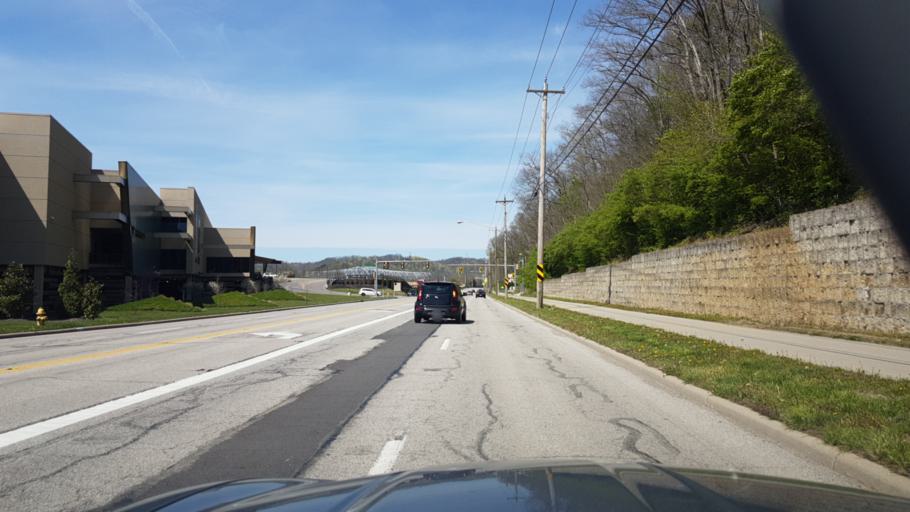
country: US
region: Kentucky
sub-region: Campbell County
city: Silver Grove
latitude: 39.0533
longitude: -84.4101
